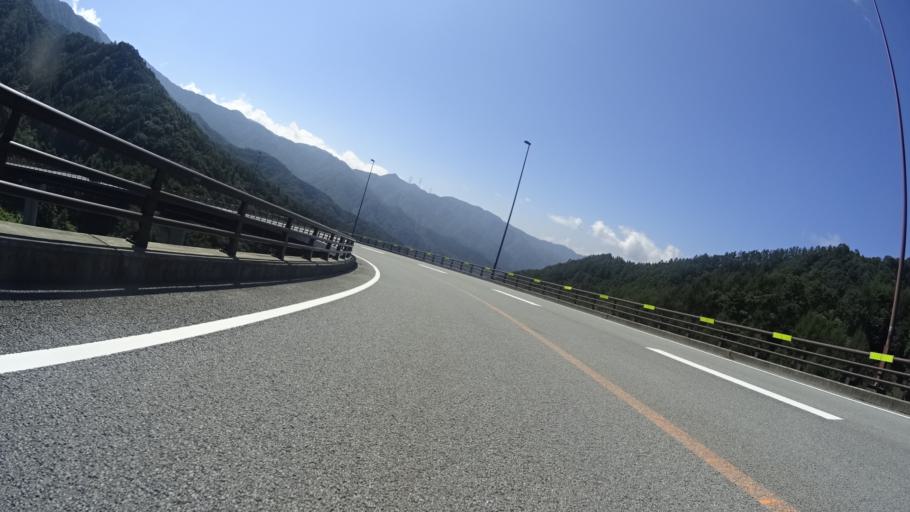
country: JP
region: Yamanashi
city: Enzan
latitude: 35.7589
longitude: 138.8057
